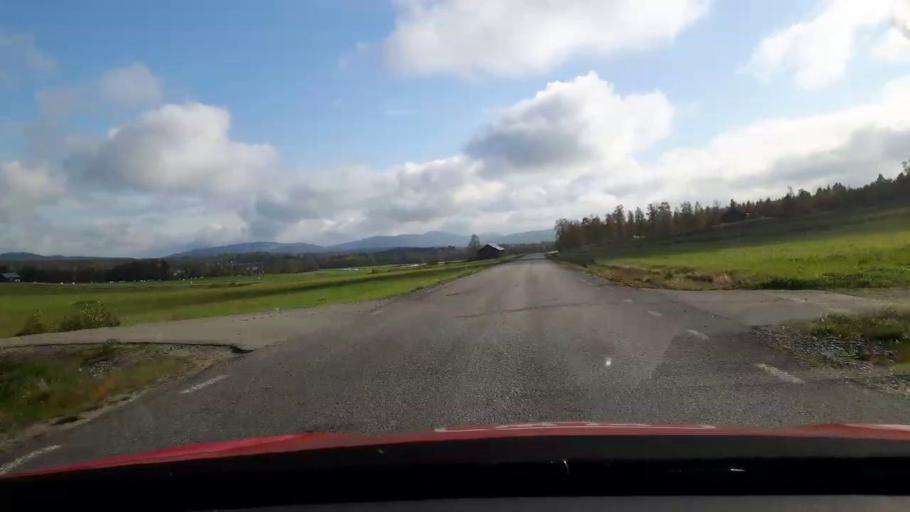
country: SE
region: Gaevleborg
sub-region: Ljusdals Kommun
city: Ljusdal
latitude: 61.7625
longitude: 16.0737
